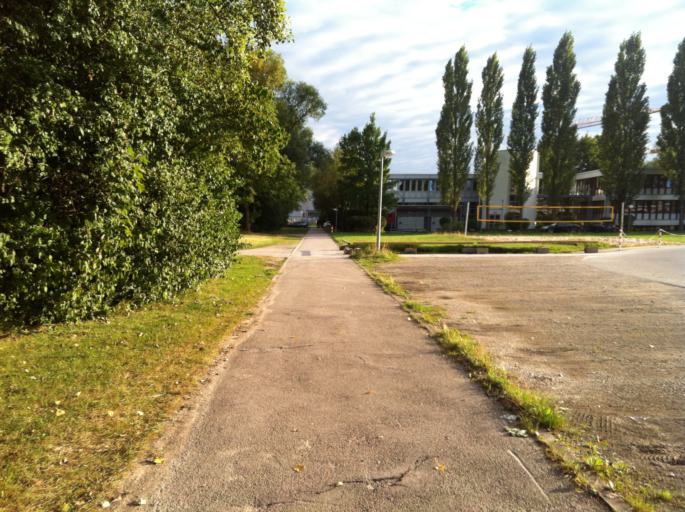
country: DE
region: Bavaria
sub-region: Upper Bavaria
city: Garching bei Munchen
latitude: 48.2684
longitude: 11.6750
